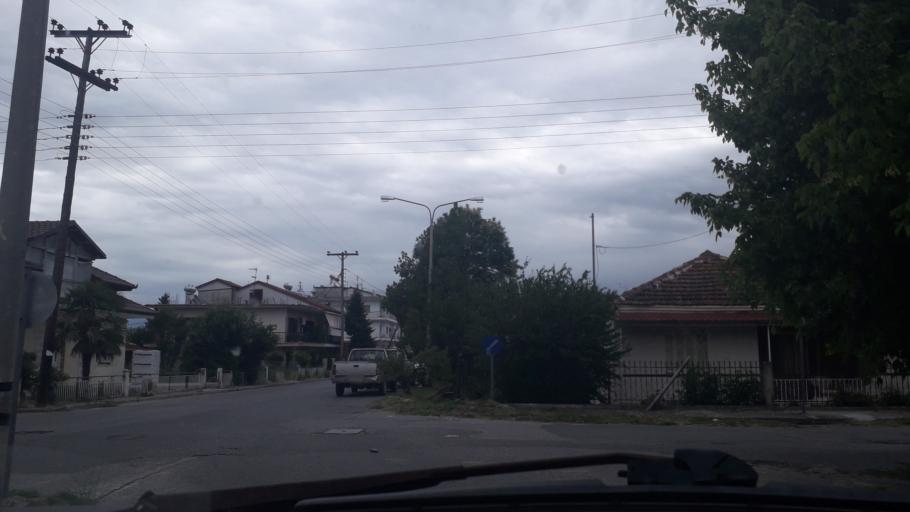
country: GR
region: Central Macedonia
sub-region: Nomos Pellis
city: Aridaia
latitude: 40.9674
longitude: 22.0592
